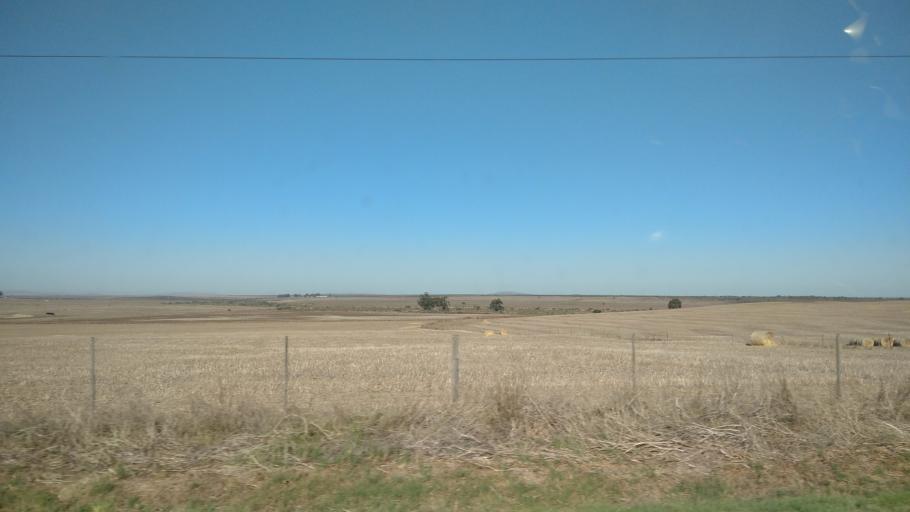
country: ZA
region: Western Cape
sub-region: West Coast District Municipality
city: Moorreesburg
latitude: -33.1213
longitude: 18.4415
